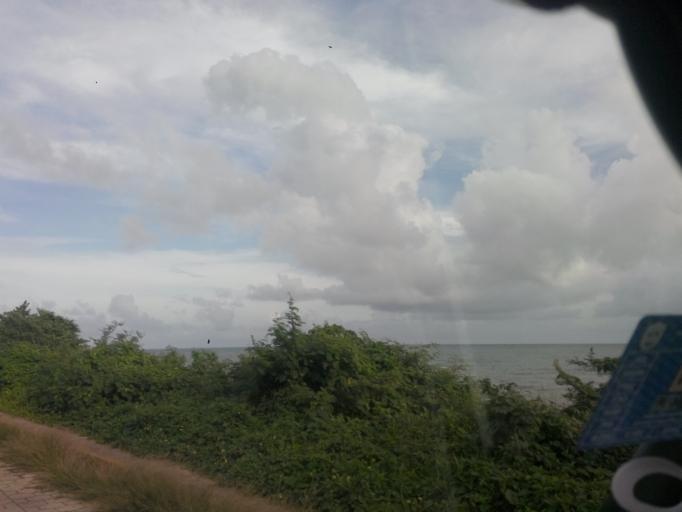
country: NI
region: Atlantico Norte (RAAN)
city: Puerto Cabezas
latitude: 14.0356
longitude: -83.3719
